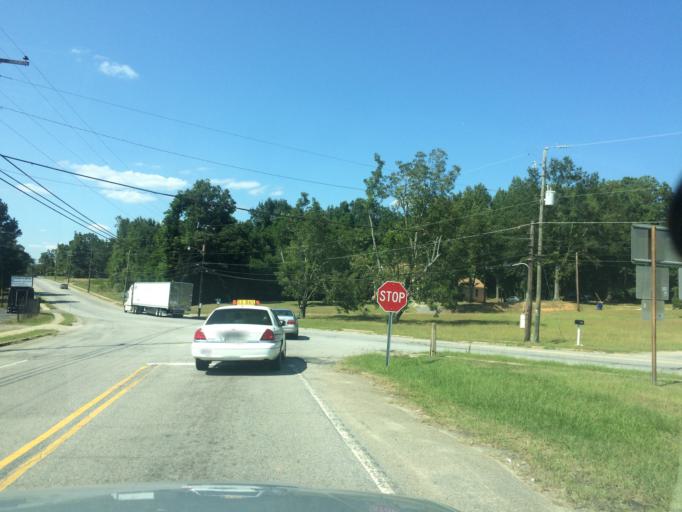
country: US
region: South Carolina
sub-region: Lexington County
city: Batesburg
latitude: 33.8993
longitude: -81.5415
